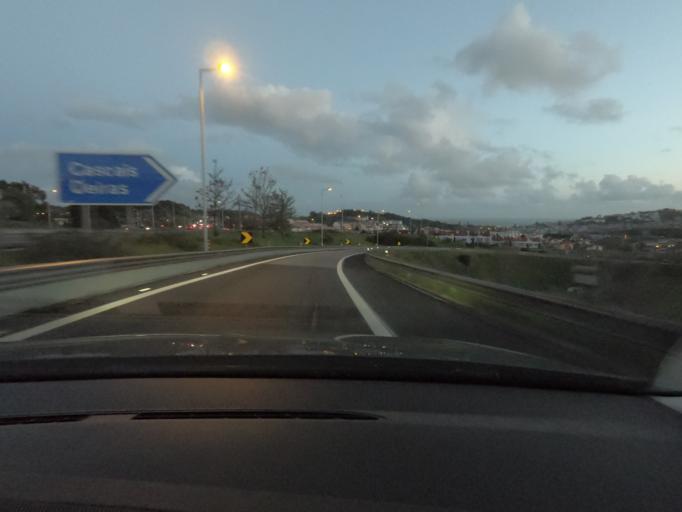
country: PT
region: Lisbon
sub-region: Oeiras
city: Quejas
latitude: 38.7180
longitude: -9.2704
